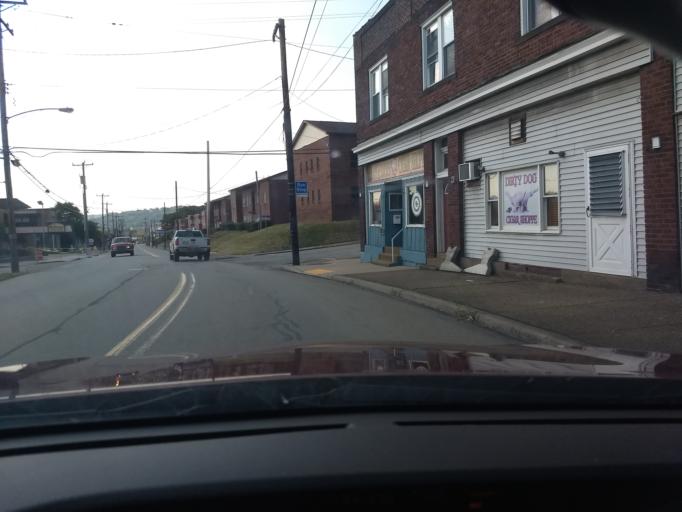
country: US
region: Pennsylvania
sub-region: Allegheny County
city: Versailles
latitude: 40.3189
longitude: -79.8343
